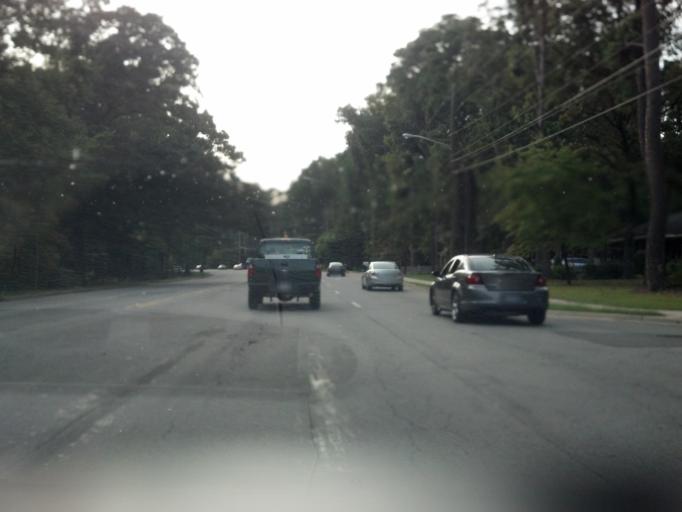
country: US
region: North Carolina
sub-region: Pitt County
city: Greenville
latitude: 35.5904
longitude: -77.3623
